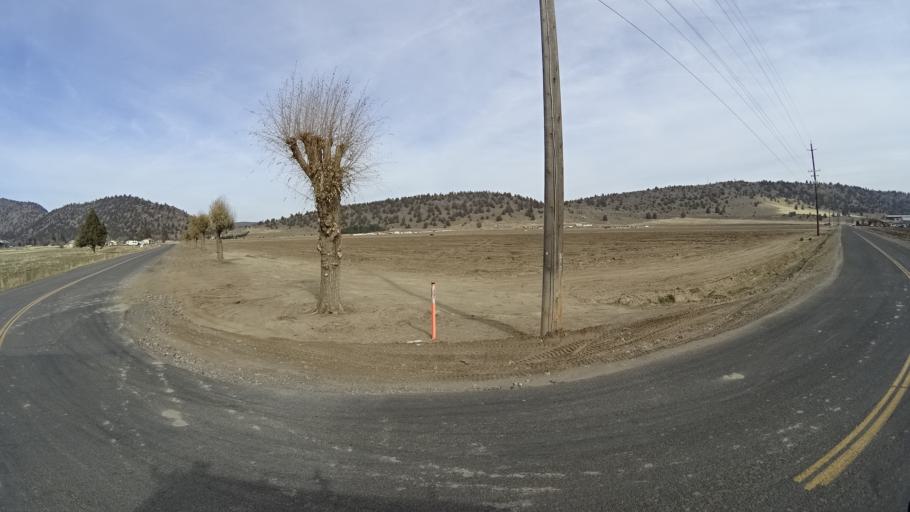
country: US
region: Oregon
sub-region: Klamath County
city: Klamath Falls
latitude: 41.9600
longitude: -121.9115
